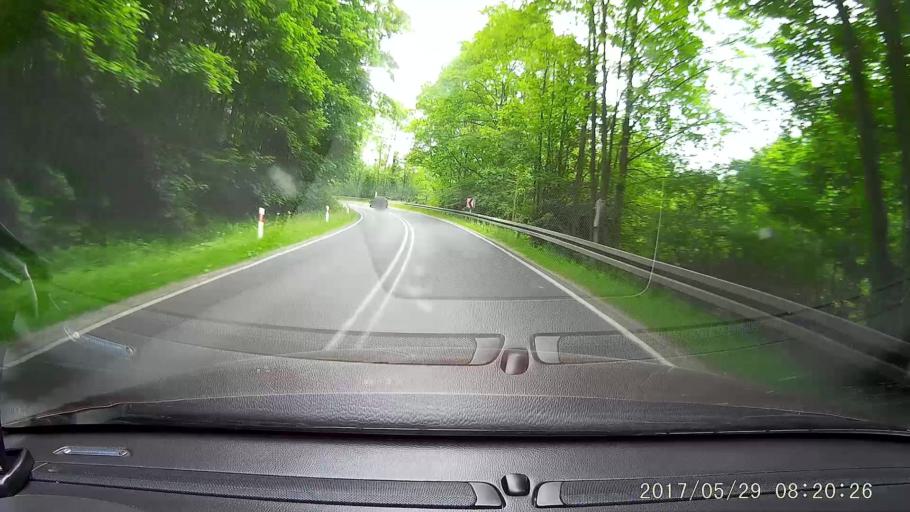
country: PL
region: Lower Silesian Voivodeship
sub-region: Powiat zlotoryjski
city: Wilkow
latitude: 51.0961
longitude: 15.8749
